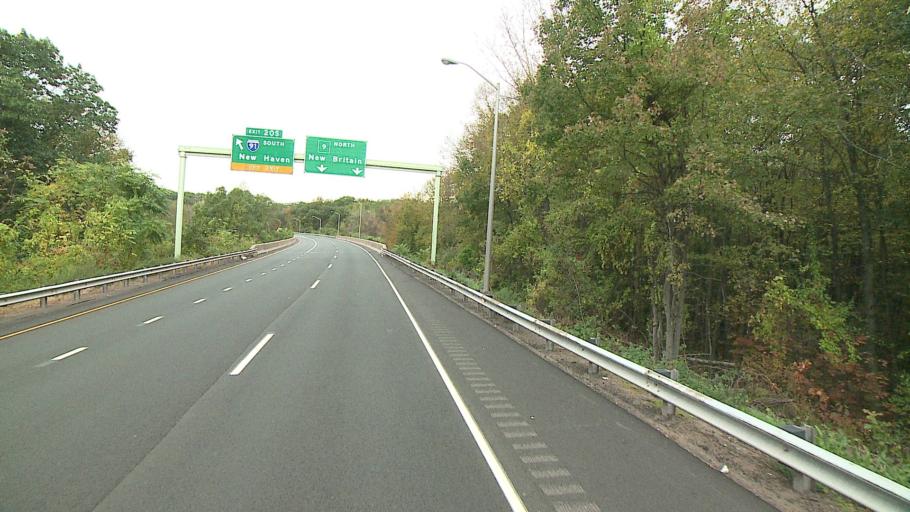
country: US
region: Connecticut
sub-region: Middlesex County
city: Cromwell
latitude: 41.6253
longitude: -72.6880
